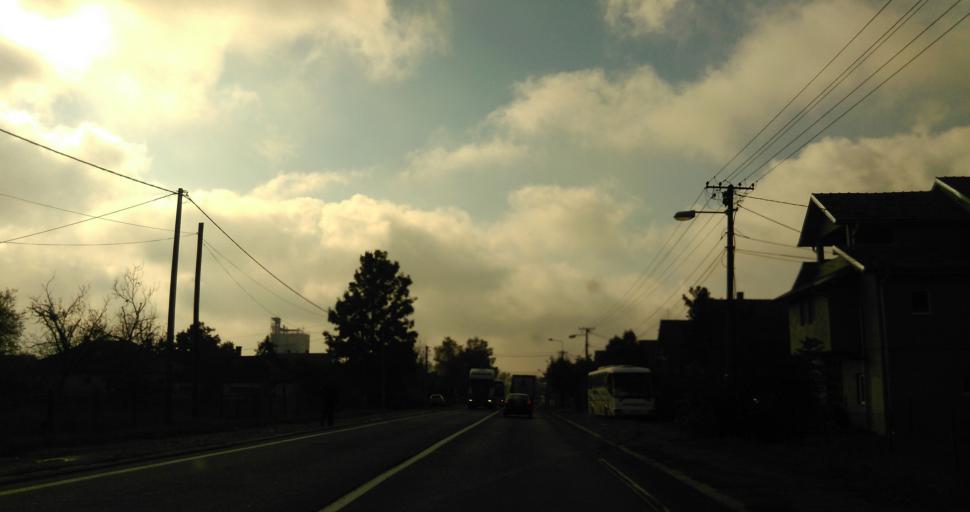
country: RS
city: Stepojevac
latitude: 44.5183
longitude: 20.2929
